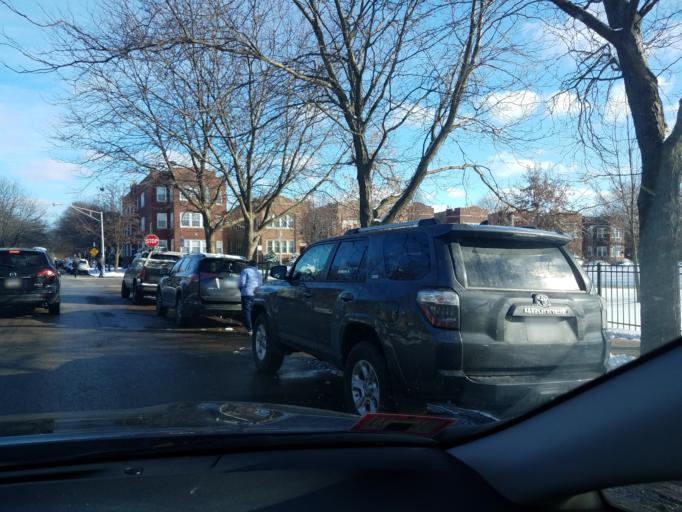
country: US
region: Illinois
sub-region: Cook County
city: Harwood Heights
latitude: 41.9569
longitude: -87.7628
